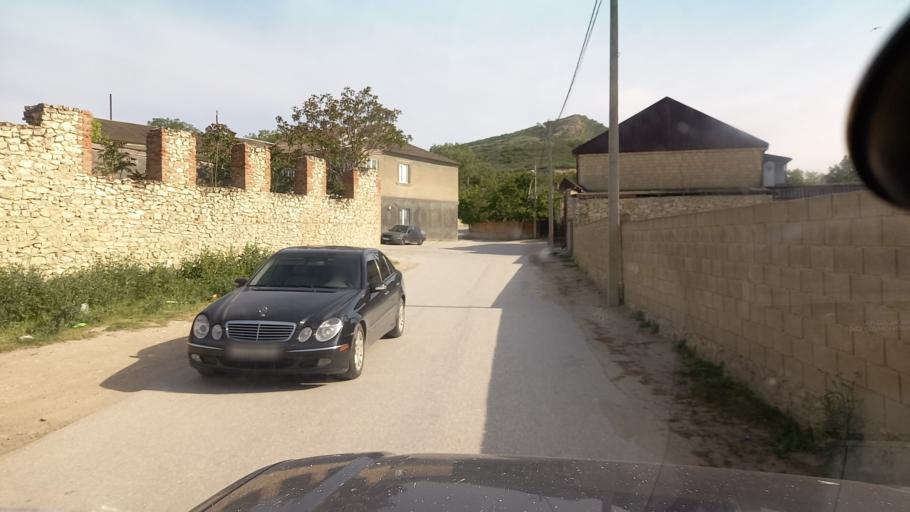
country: RU
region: Dagestan
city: Karabudakhkent
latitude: 42.7100
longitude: 47.5693
